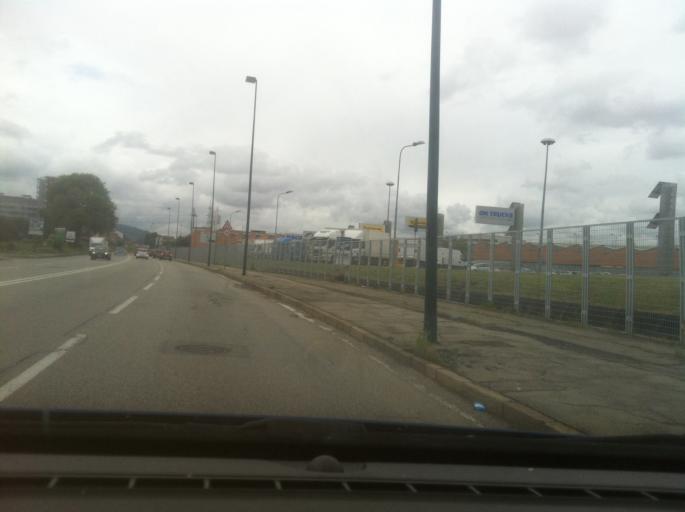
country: IT
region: Piedmont
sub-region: Provincia di Torino
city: San Mauro Torinese
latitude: 45.1118
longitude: 7.7298
